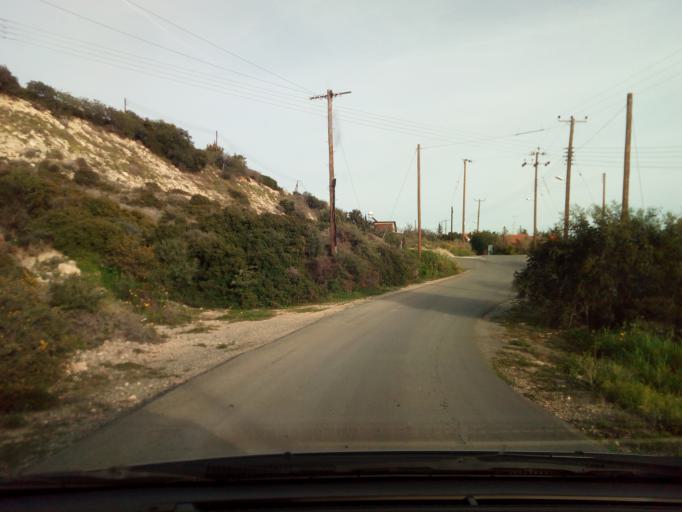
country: CY
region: Larnaka
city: Agios Tychon
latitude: 34.7222
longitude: 33.1320
